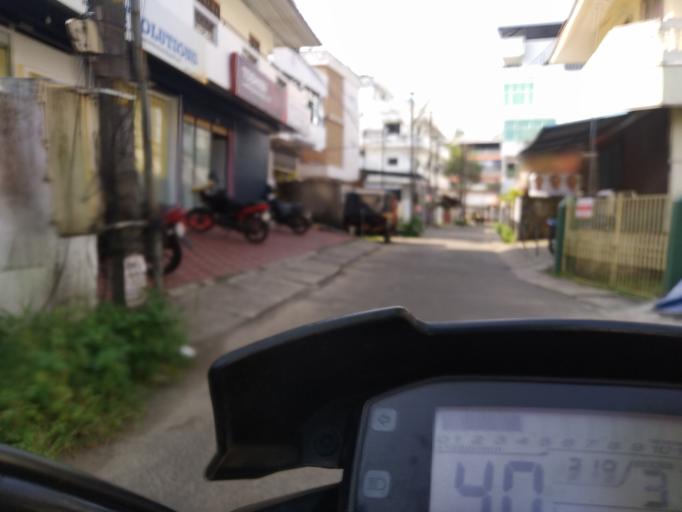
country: IN
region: Kerala
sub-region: Ernakulam
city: Cochin
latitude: 9.9826
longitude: 76.2933
